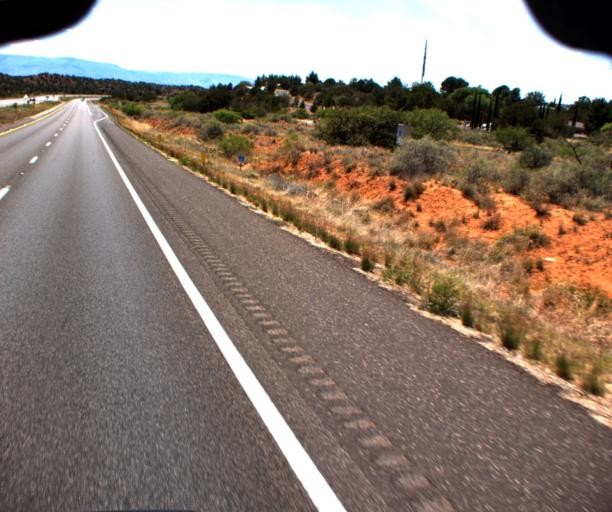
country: US
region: Arizona
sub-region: Yavapai County
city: West Sedona
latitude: 34.8427
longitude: -111.8636
